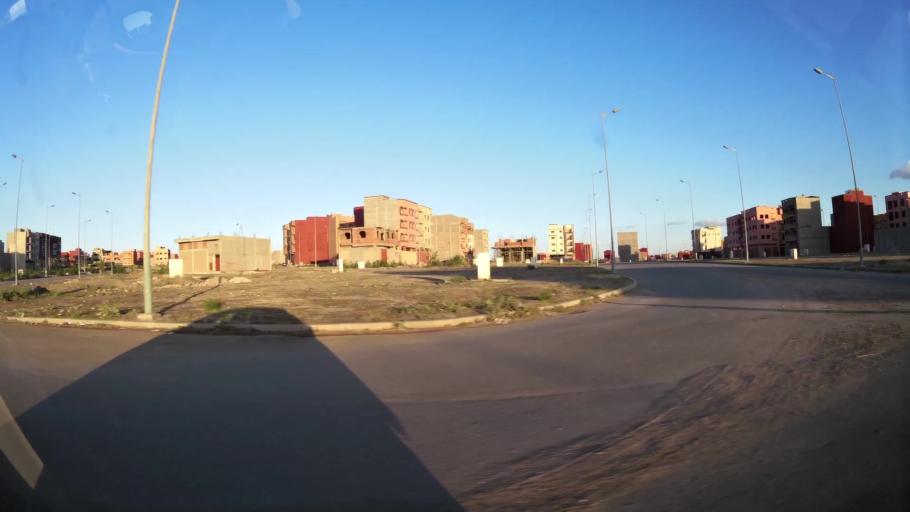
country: MA
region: Marrakech-Tensift-Al Haouz
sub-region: Kelaa-Des-Sraghna
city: Sidi Abdallah
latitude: 32.2400
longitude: -7.9448
